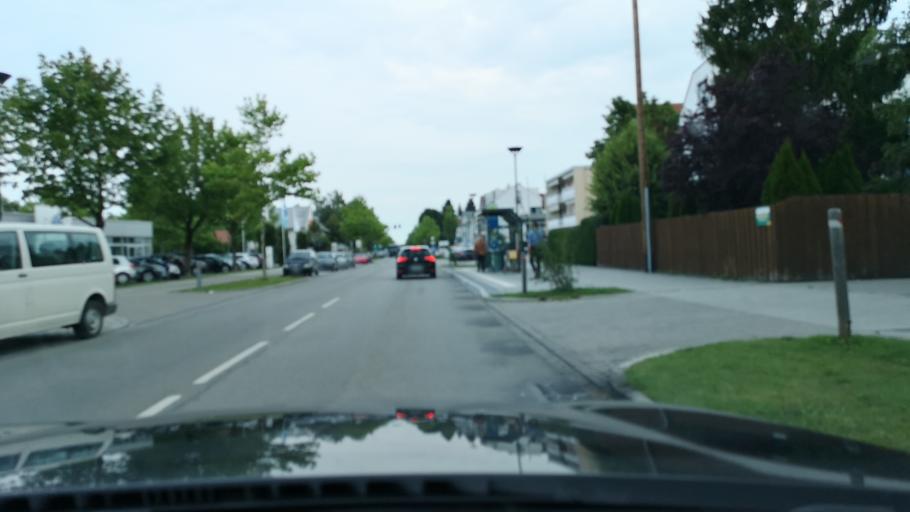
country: DE
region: Bavaria
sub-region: Upper Bavaria
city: Ottobrunn
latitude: 48.0555
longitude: 11.6679
